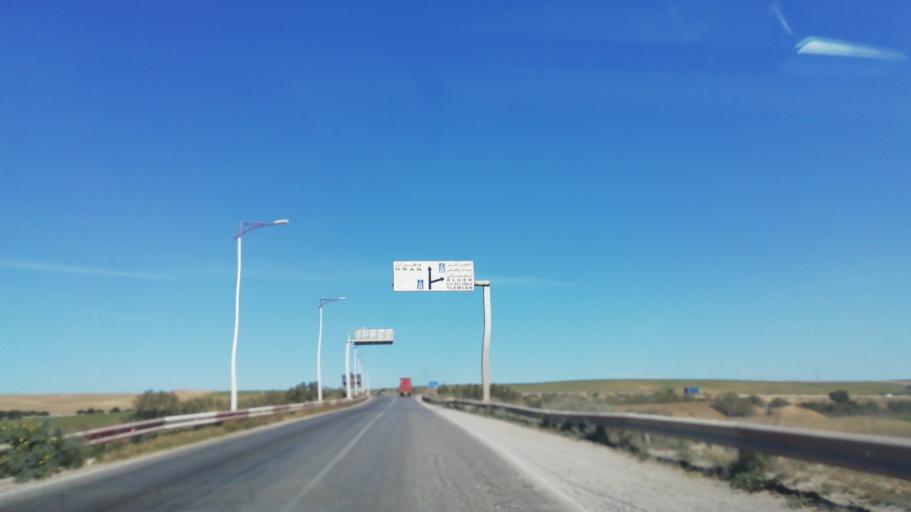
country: DZ
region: Oran
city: Sidi ech Chahmi
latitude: 35.5708
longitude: -0.5579
